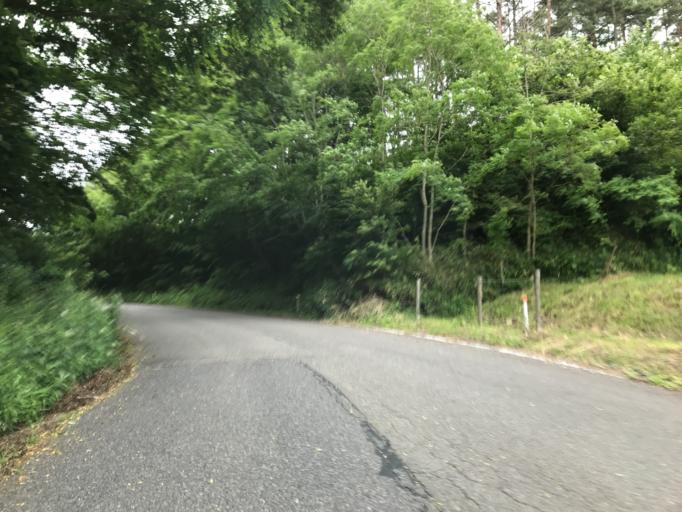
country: JP
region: Fukushima
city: Funehikimachi-funehiki
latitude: 37.3975
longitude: 140.6787
